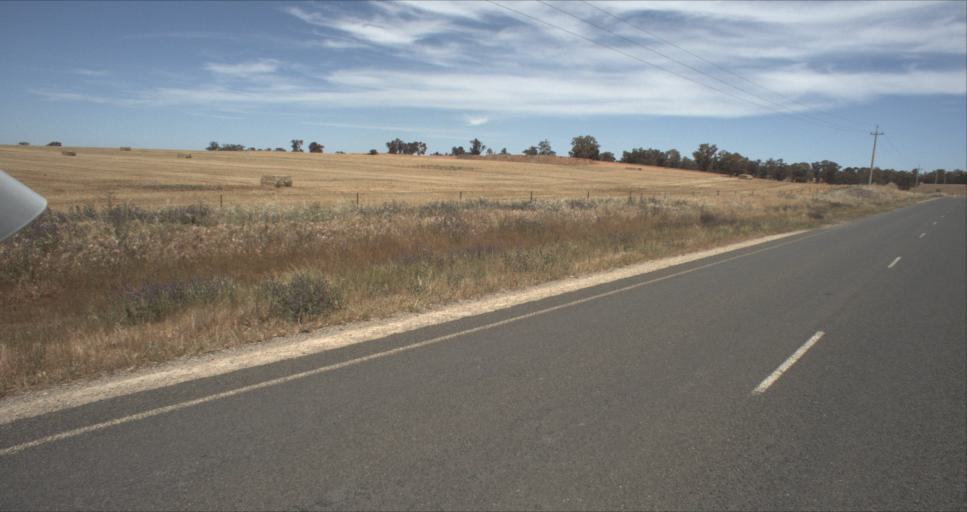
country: AU
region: New South Wales
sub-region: Leeton
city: Leeton
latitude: -34.6549
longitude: 146.4604
